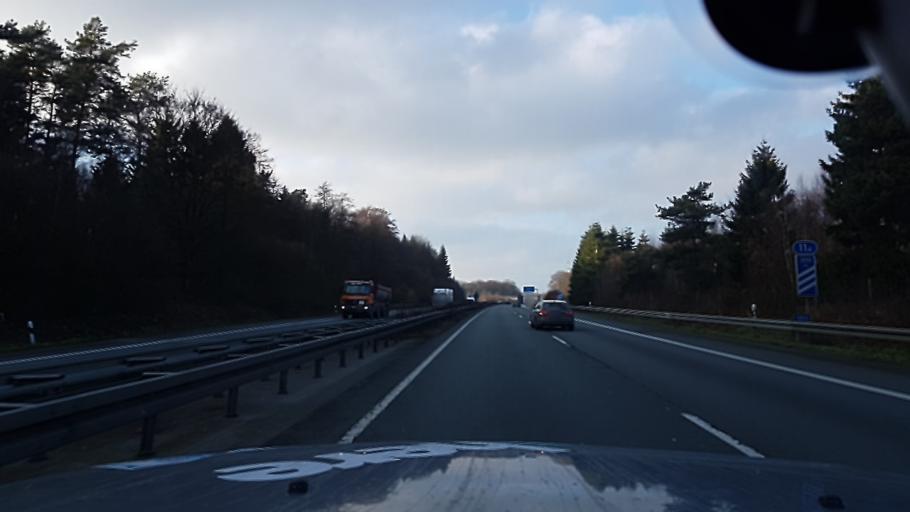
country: DE
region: North Rhine-Westphalia
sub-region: Regierungsbezirk Munster
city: Birgte
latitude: 52.2678
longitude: 7.6662
